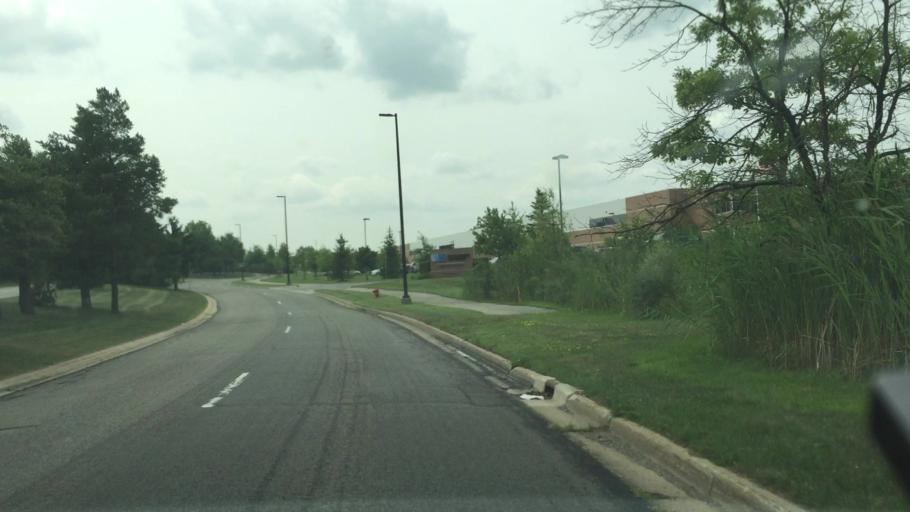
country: US
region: Michigan
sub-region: Oakland County
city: Auburn Hills
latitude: 42.6663
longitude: -83.2358
